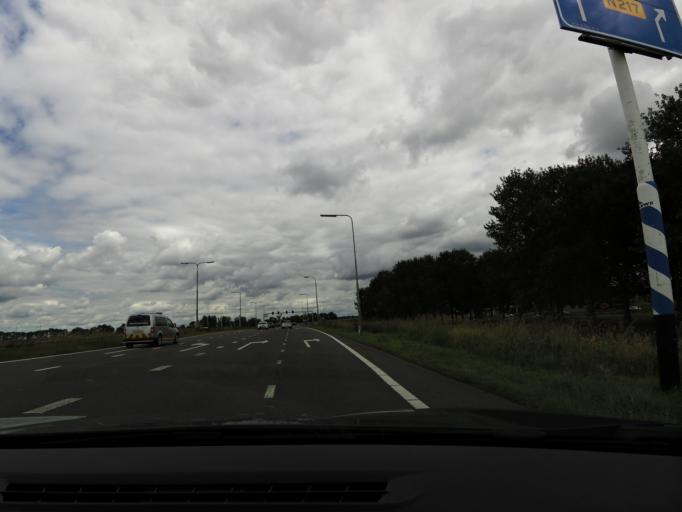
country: NL
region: South Holland
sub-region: Gemeente Binnenmaas
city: Heinenoord
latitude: 51.8166
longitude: 4.4871
